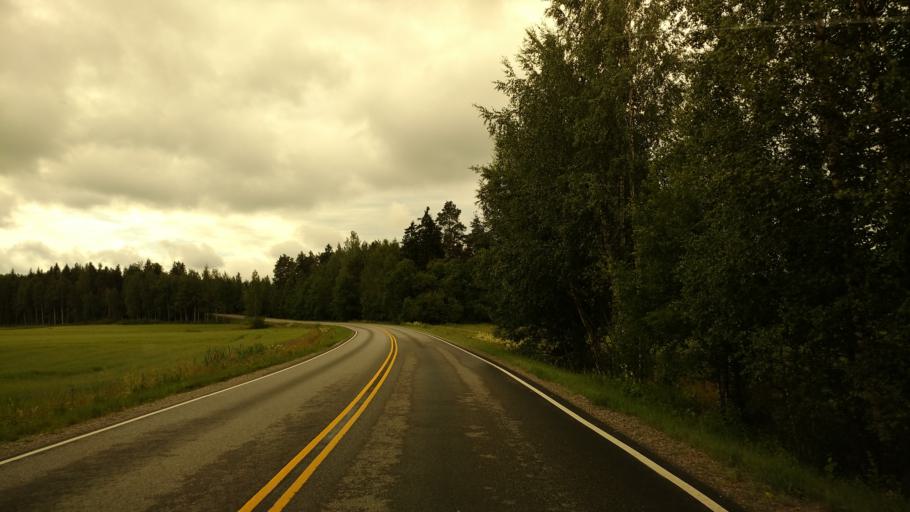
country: FI
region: Varsinais-Suomi
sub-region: Salo
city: Kuusjoki
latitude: 60.4466
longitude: 23.1761
